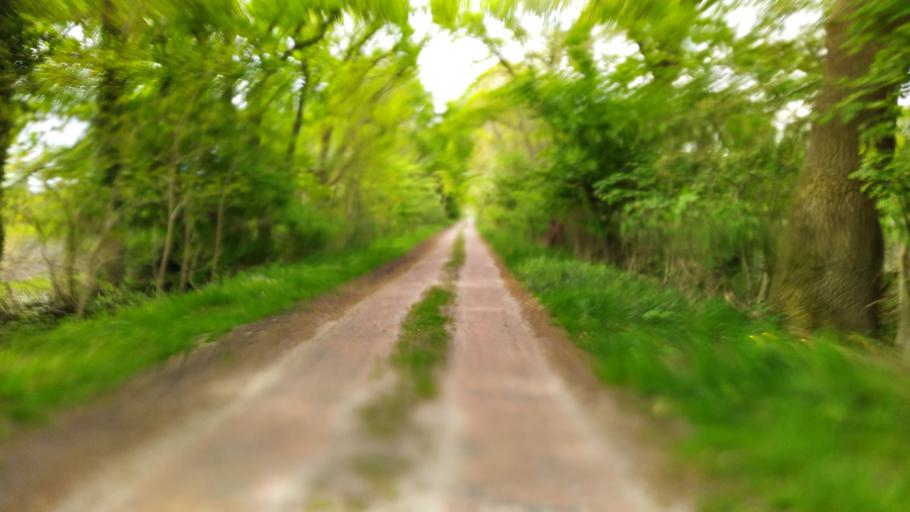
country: DE
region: Lower Saxony
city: Farven
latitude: 53.4304
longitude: 9.3358
